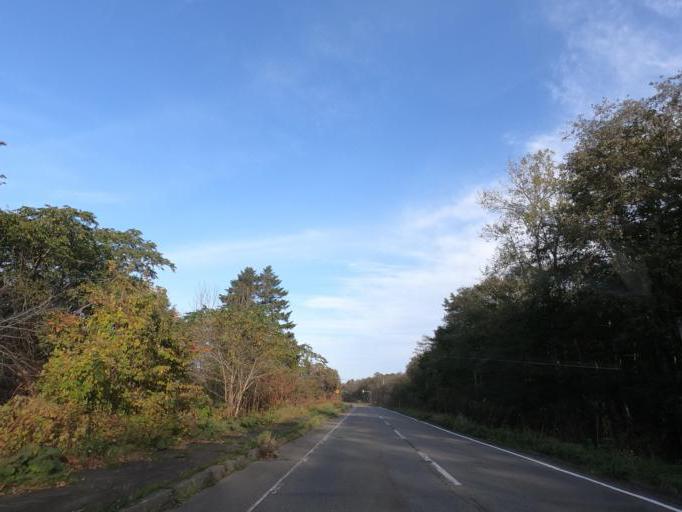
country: JP
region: Hokkaido
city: Obihiro
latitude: 42.5010
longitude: 143.4112
